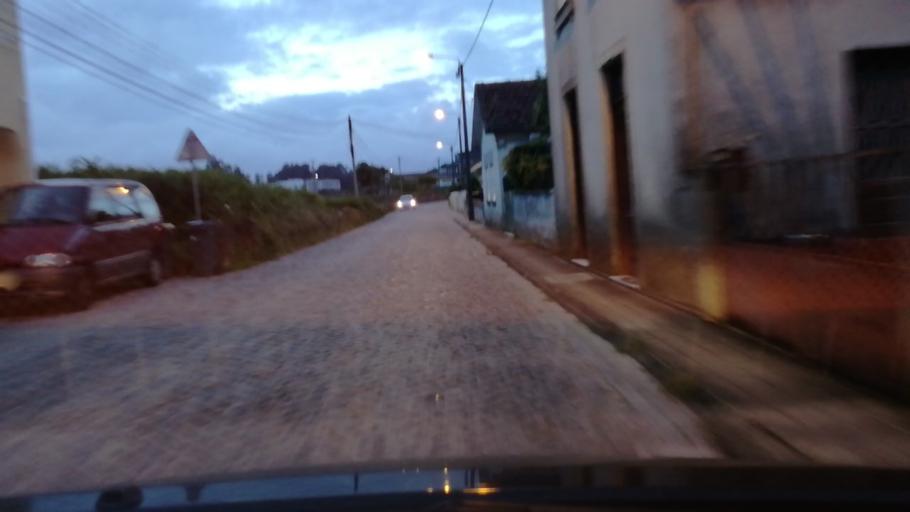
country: PT
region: Porto
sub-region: Maia
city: Maia
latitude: 41.2521
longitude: -8.6092
